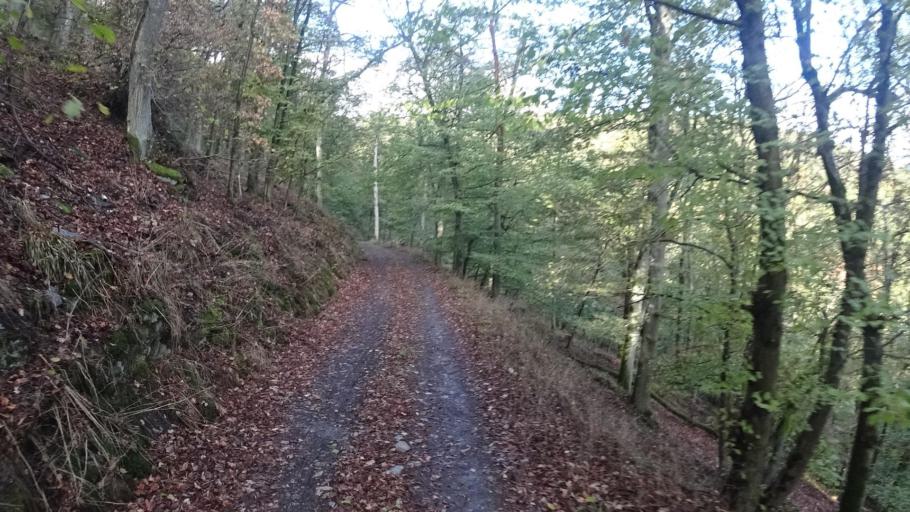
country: DE
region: Rheinland-Pfalz
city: Kamp-Bornhofen
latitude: 50.2015
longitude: 7.6046
